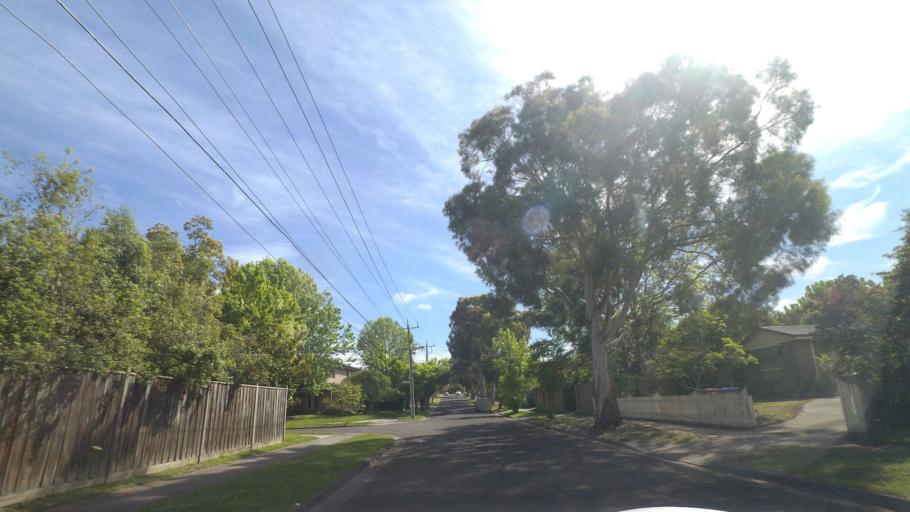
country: AU
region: Victoria
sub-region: Knox
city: Bayswater
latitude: -37.8540
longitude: 145.2500
